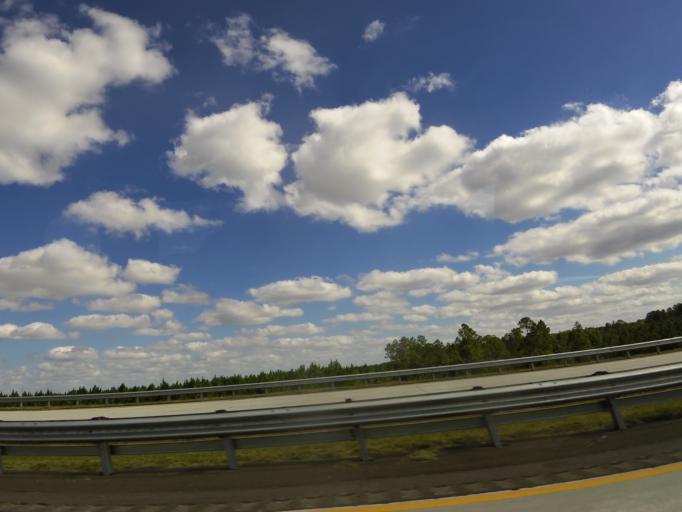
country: US
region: Florida
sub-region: Saint Johns County
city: Fruit Cove
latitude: 30.0888
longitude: -81.5204
